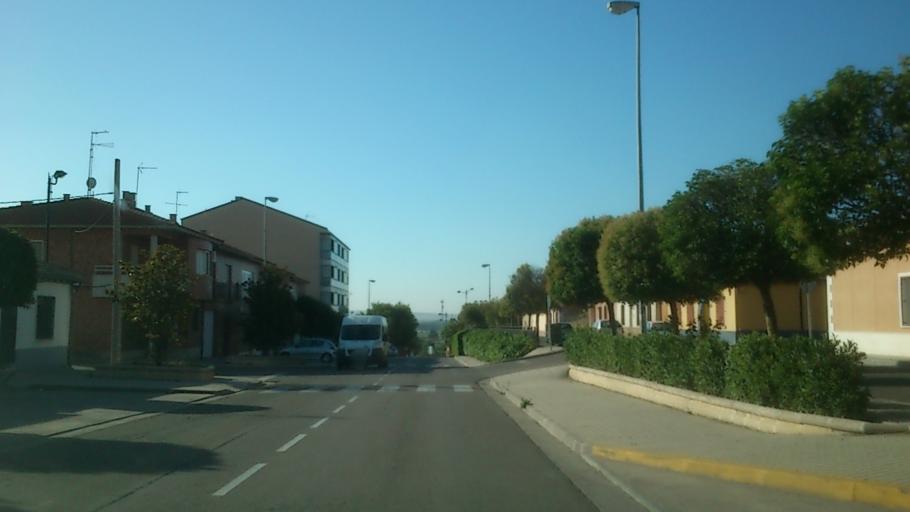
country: ES
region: Aragon
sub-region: Provincia de Zaragoza
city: Villanueva de Gallego
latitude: 41.7727
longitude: -0.8239
